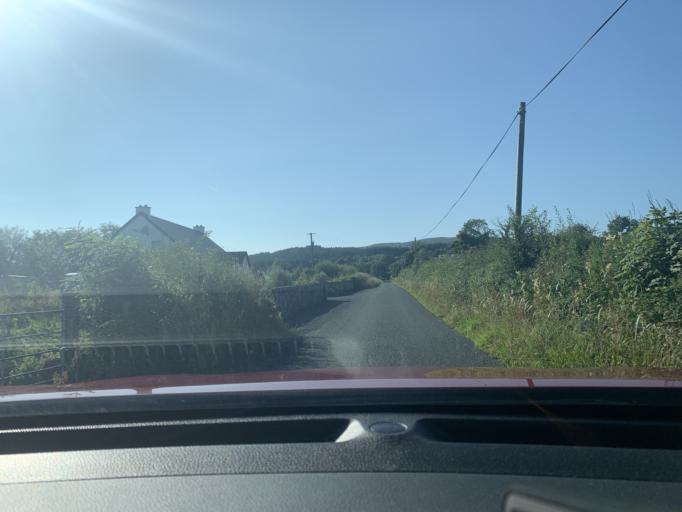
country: IE
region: Connaught
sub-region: Sligo
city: Tobercurry
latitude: 54.0813
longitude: -8.8119
